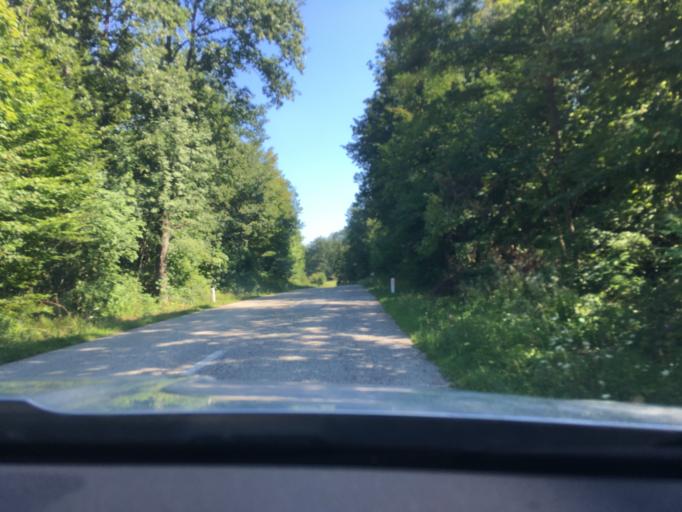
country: SI
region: Metlika
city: Metlika
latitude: 45.5024
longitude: 15.3417
